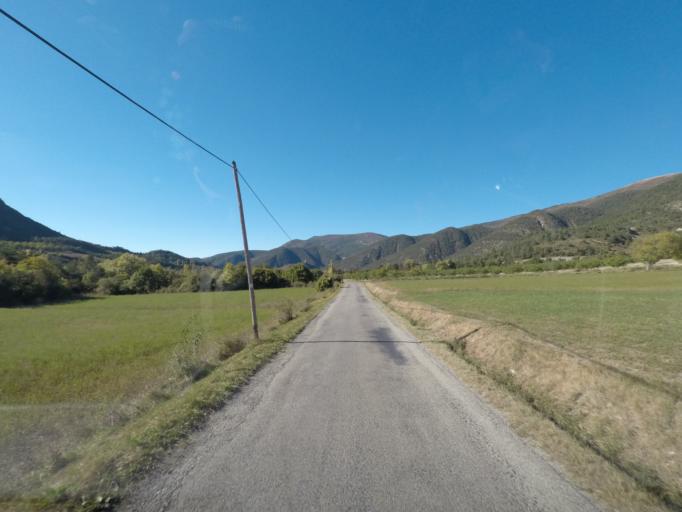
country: FR
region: Provence-Alpes-Cote d'Azur
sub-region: Departement des Hautes-Alpes
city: Serres
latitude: 44.4585
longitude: 5.5284
